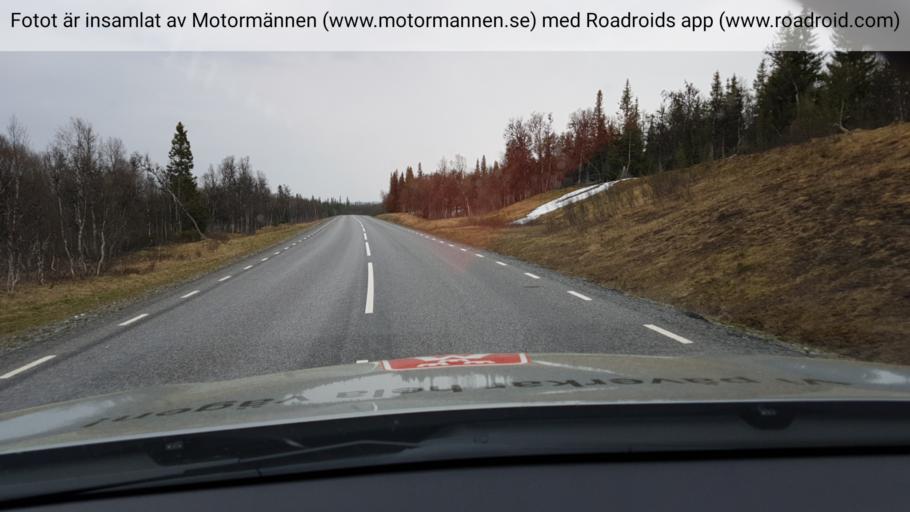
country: NO
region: Nord-Trondelag
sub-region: Meraker
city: Meraker
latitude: 63.5608
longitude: 12.3005
